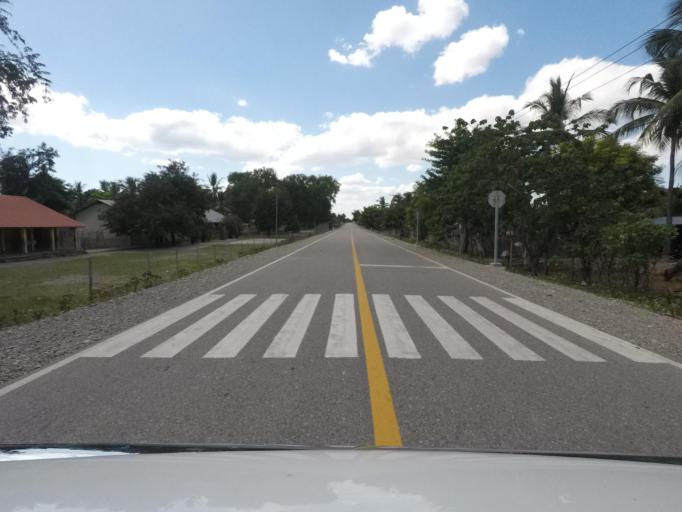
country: TL
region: Baucau
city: Baucau
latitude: -8.4318
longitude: 126.6782
